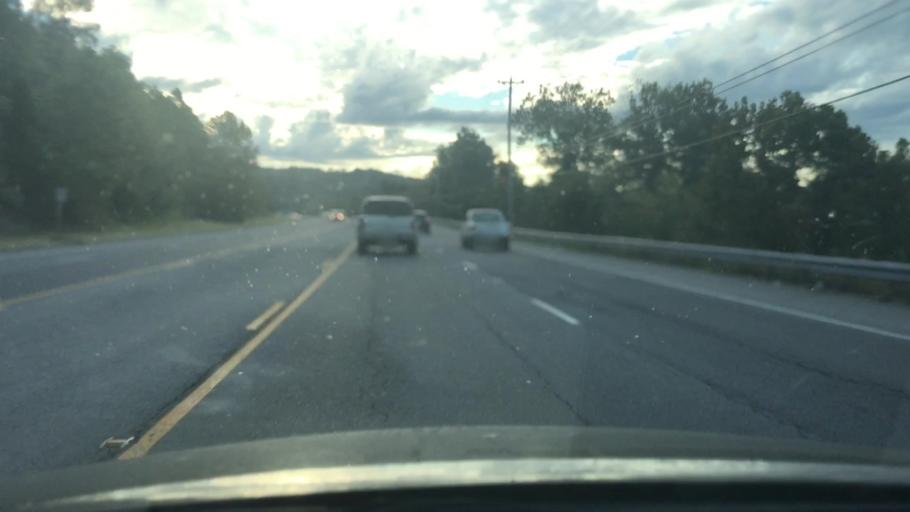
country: US
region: Tennessee
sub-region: Cheatham County
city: Ashland City
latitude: 36.2622
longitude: -87.0553
